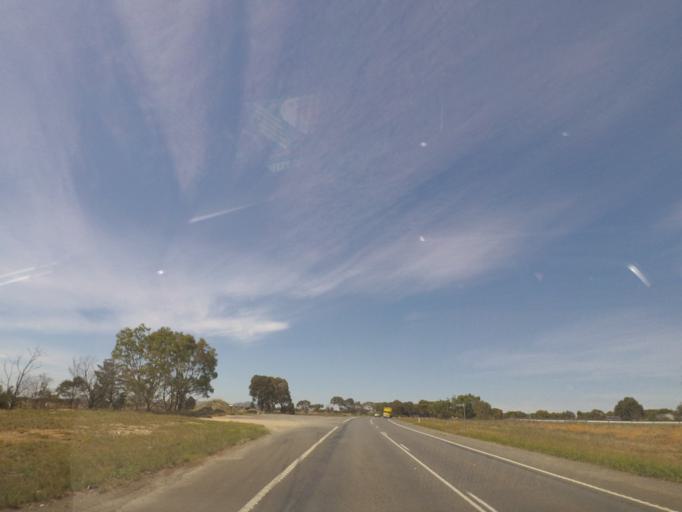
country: AU
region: Victoria
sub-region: Wyndham
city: Wyndham Vale
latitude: -37.8566
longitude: 144.3876
